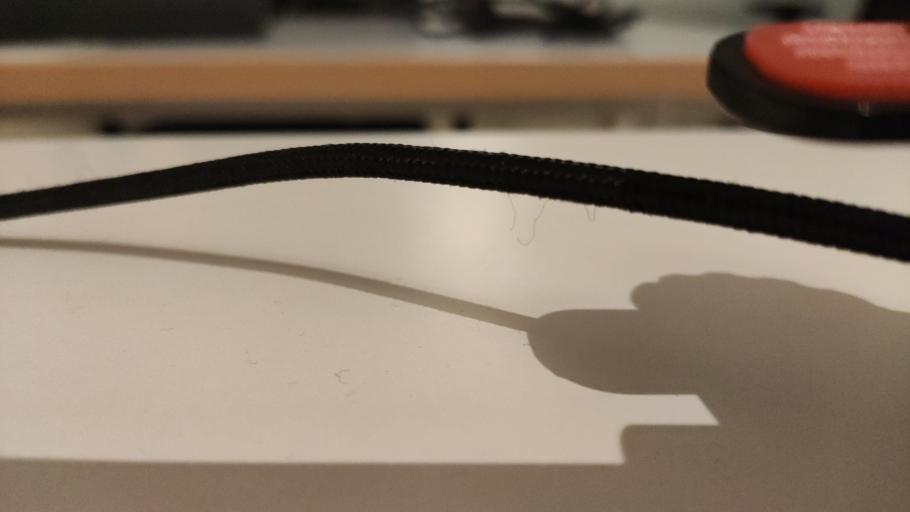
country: RU
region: Moskovskaya
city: Kurovskoye
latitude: 55.5810
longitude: 38.8893
